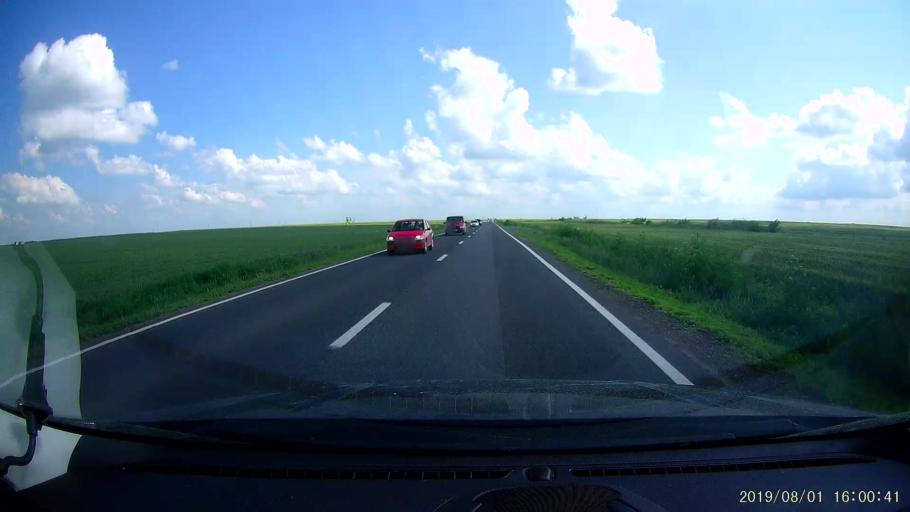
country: RO
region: Ialomita
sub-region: Comuna Ciulnita
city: Ciulnita
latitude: 44.5236
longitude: 27.3892
